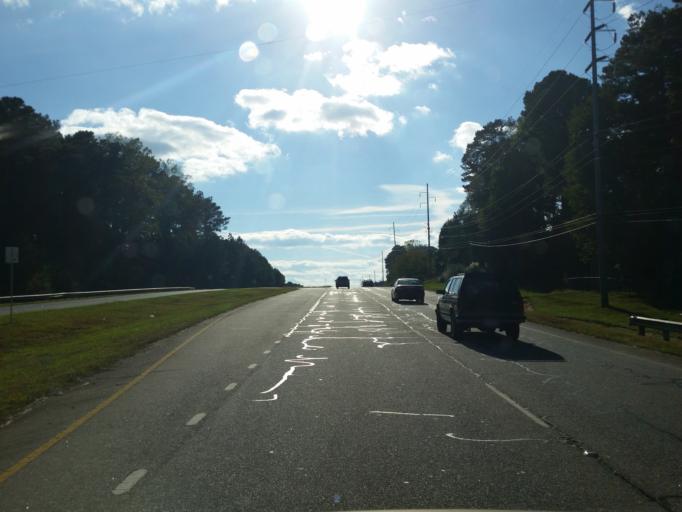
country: US
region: Georgia
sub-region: Paulding County
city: Hiram
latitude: 33.9298
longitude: -84.7395
